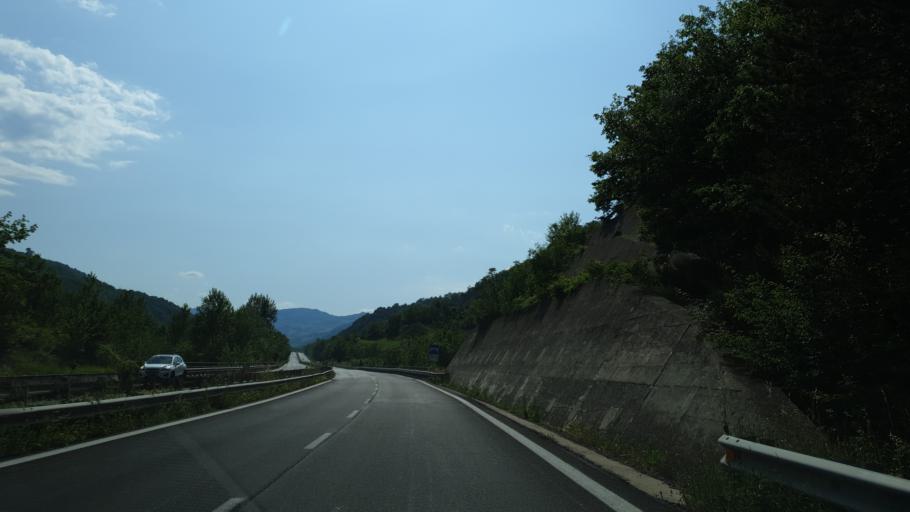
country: IT
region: Emilia-Romagna
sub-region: Forli-Cesena
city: San Piero in Bagno
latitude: 43.8912
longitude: 12.0437
